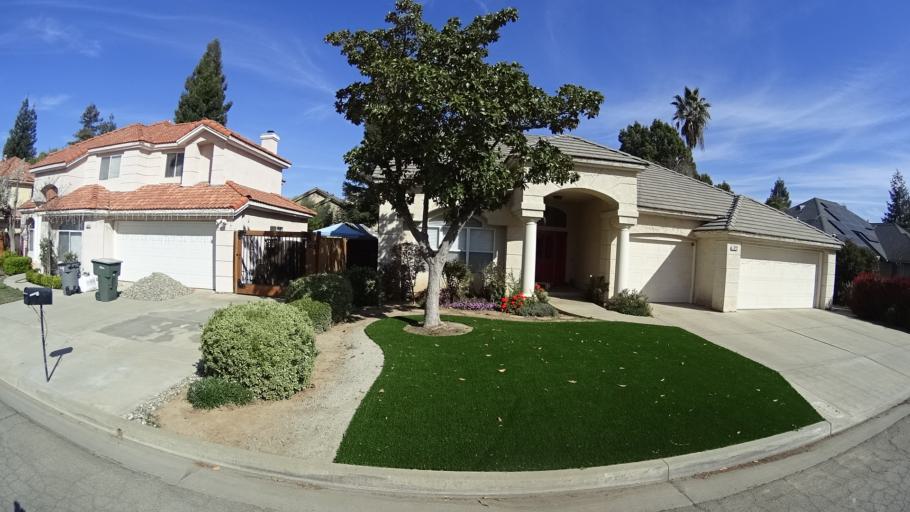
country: US
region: California
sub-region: Fresno County
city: Clovis
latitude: 36.8542
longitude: -119.7505
